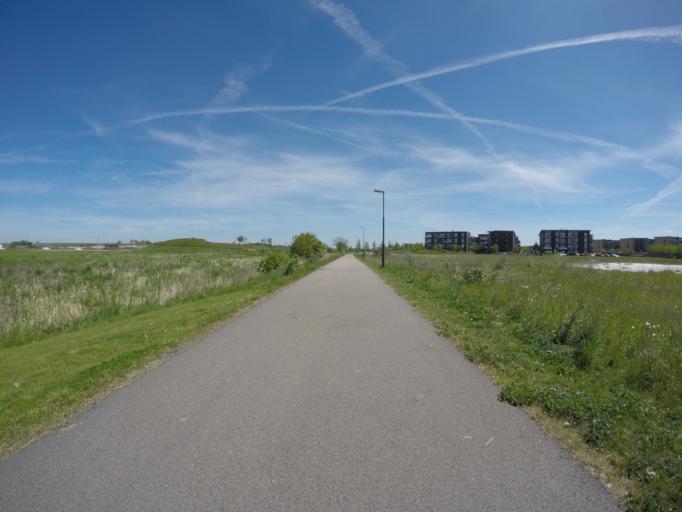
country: SE
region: Skane
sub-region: Malmo
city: Bunkeflostrand
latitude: 55.5612
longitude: 12.9282
